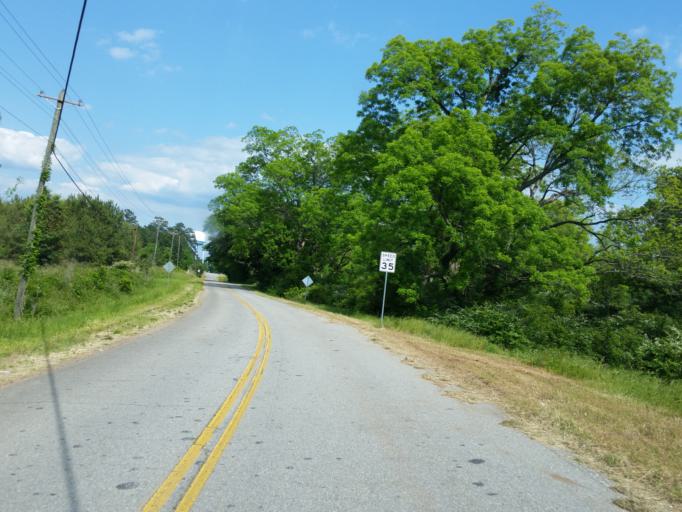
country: US
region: Georgia
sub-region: Houston County
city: Perry
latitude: 32.4900
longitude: -83.7358
